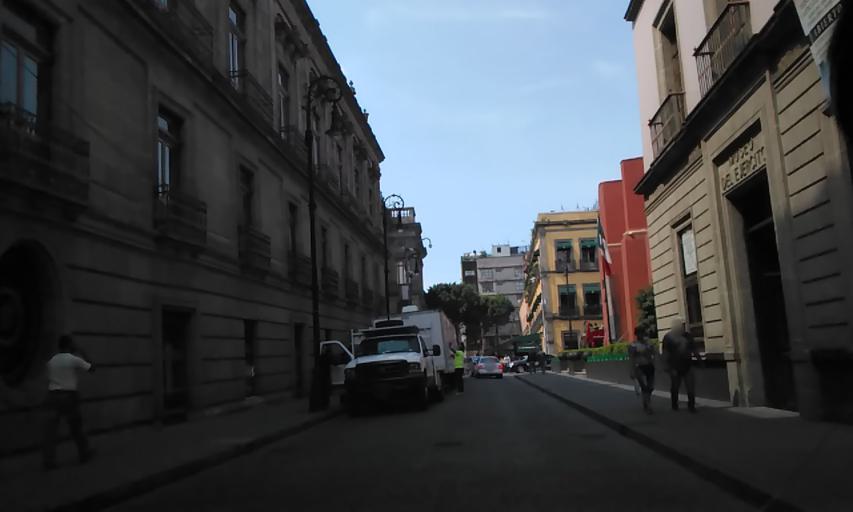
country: MX
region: Mexico City
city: Cuauhtemoc
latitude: 19.4353
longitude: -99.1391
